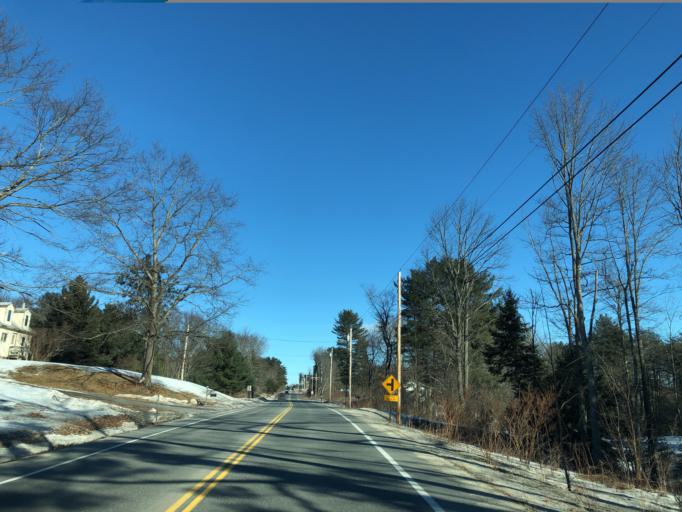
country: US
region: Maine
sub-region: Cumberland County
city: South Windham
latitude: 43.7646
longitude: -70.4397
